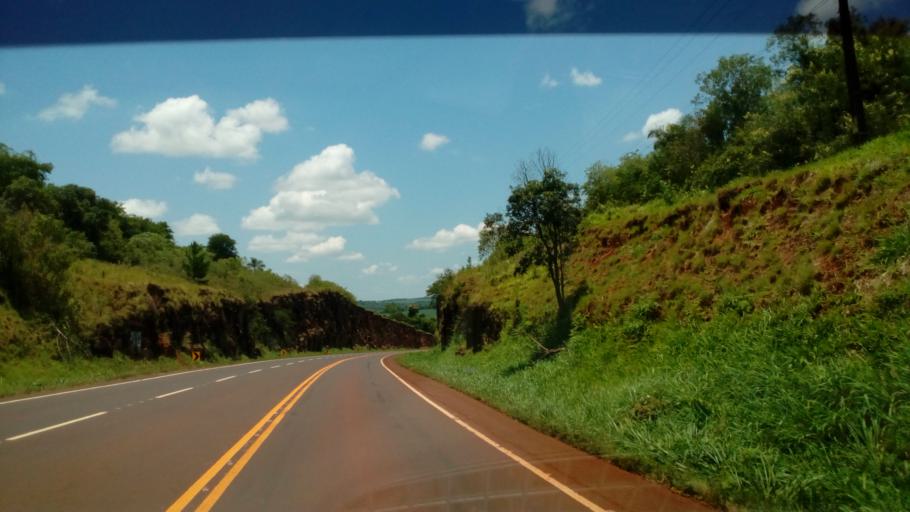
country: PY
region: Itapua
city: Arquitecto Tomas Romero Pereira
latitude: -26.4070
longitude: -55.2245
